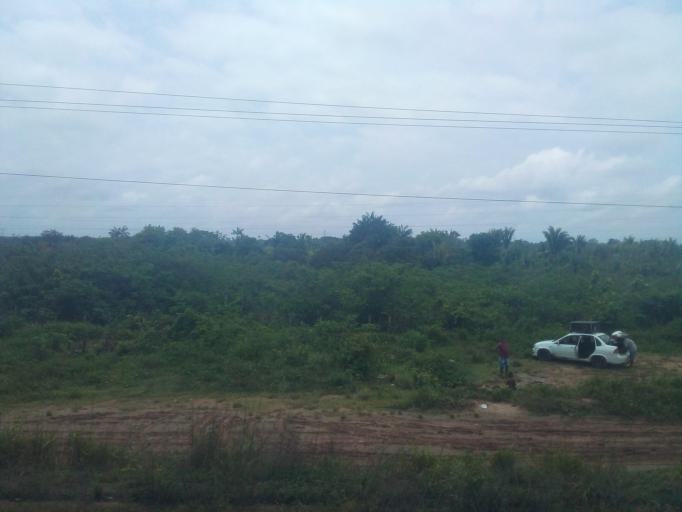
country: BR
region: Maranhao
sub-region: Vitoria Do Mearim
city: Vitoria do Mearim
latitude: -3.5818
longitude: -44.9541
